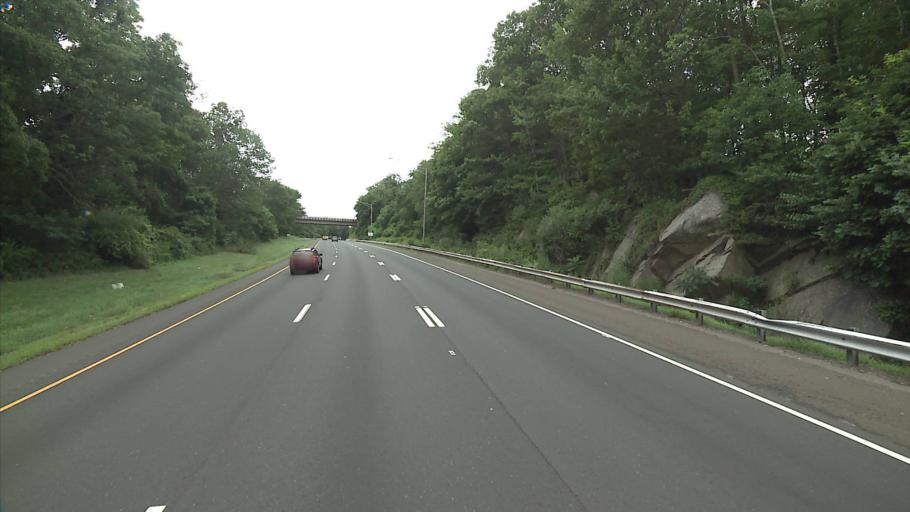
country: US
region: Connecticut
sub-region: Fairfield County
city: Shelton
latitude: 41.2963
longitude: -73.1057
